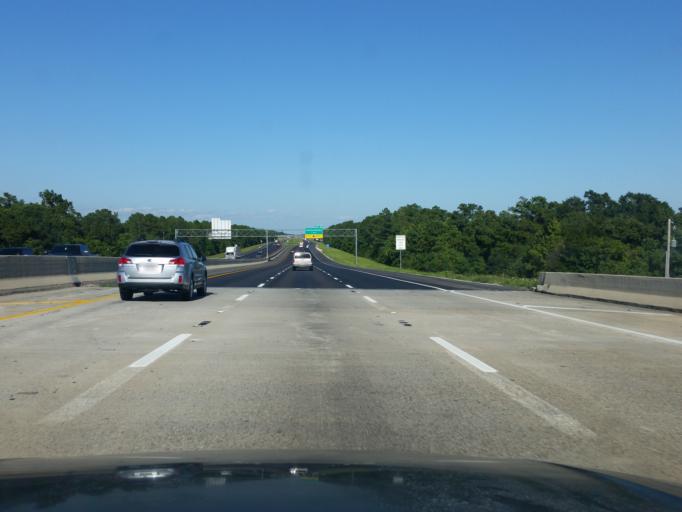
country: US
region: Mississippi
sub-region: Hancock County
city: Diamondhead
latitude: 30.3659
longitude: -89.3986
